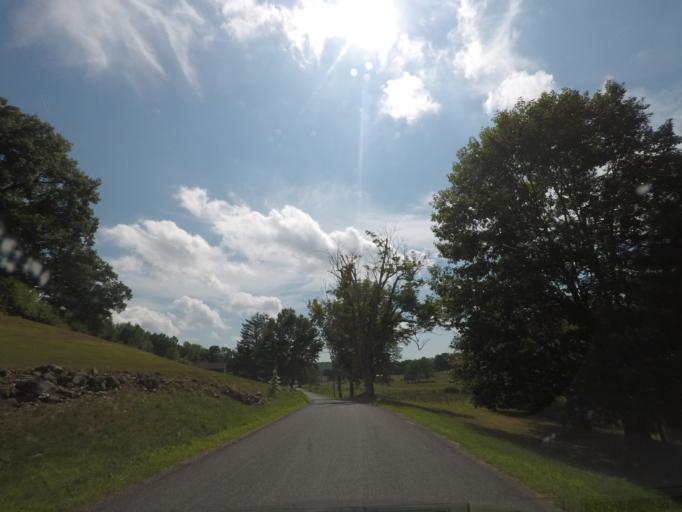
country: US
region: New York
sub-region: Rensselaer County
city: Averill Park
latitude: 42.5823
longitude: -73.5292
